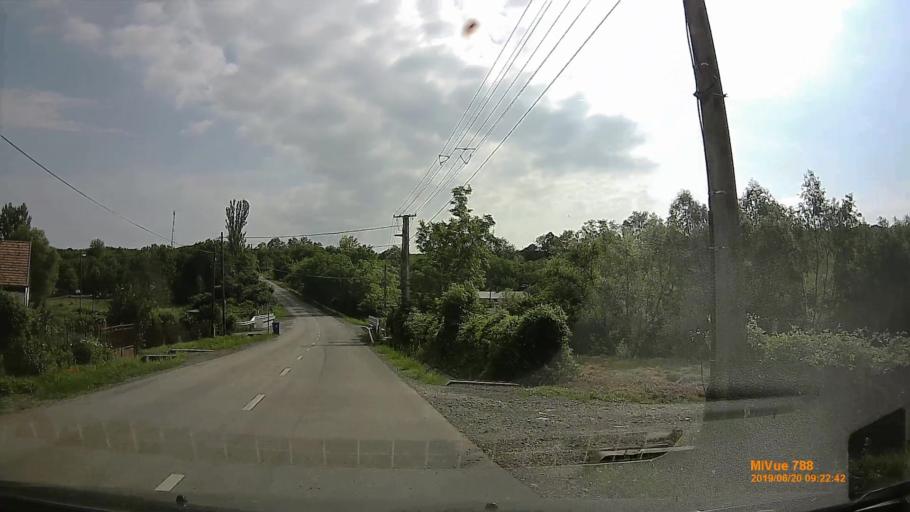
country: HU
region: Baranya
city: Hosszuheteny
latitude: 46.1211
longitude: 18.3425
